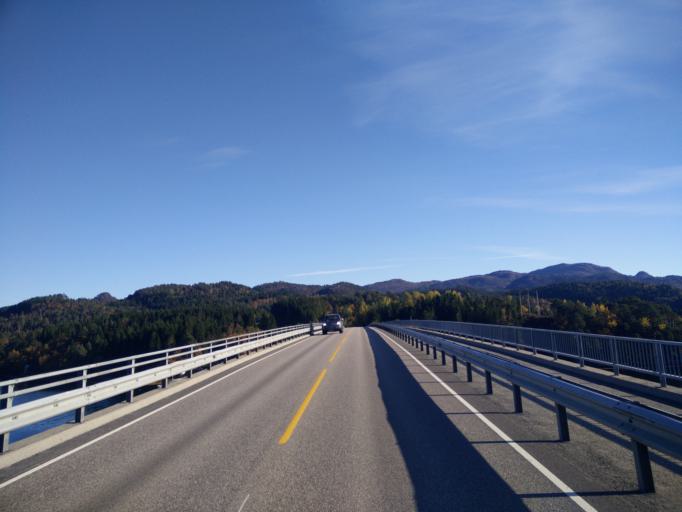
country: NO
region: More og Romsdal
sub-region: Kristiansund
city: Rensvik
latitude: 63.0127
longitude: 7.9855
